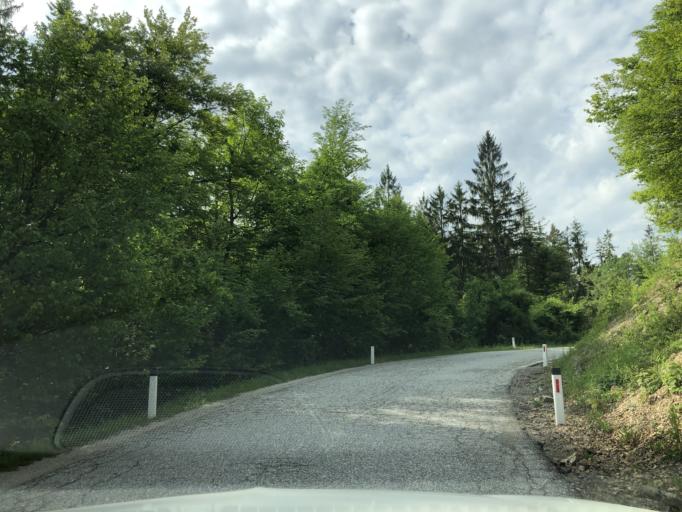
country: SI
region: Bloke
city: Nova Vas
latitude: 45.7997
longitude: 14.5555
